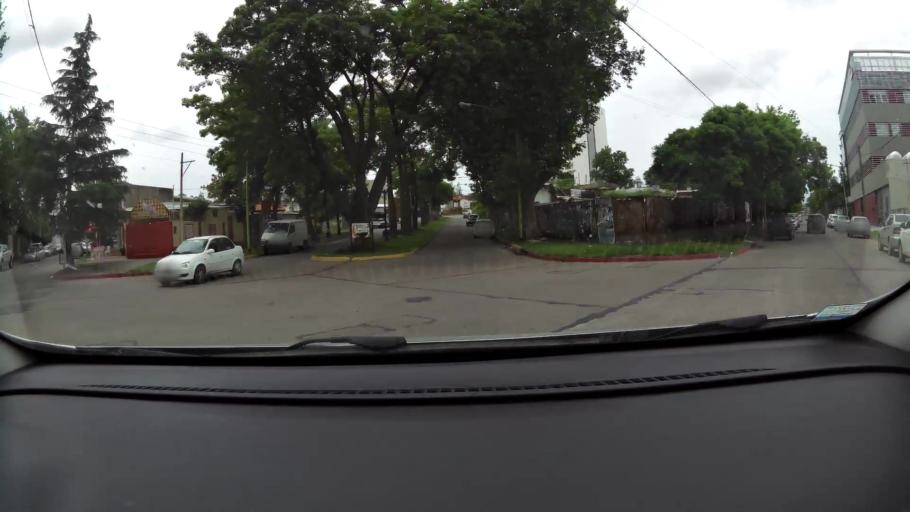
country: AR
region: Buenos Aires
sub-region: Partido de Campana
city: Campana
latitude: -34.1615
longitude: -58.9567
